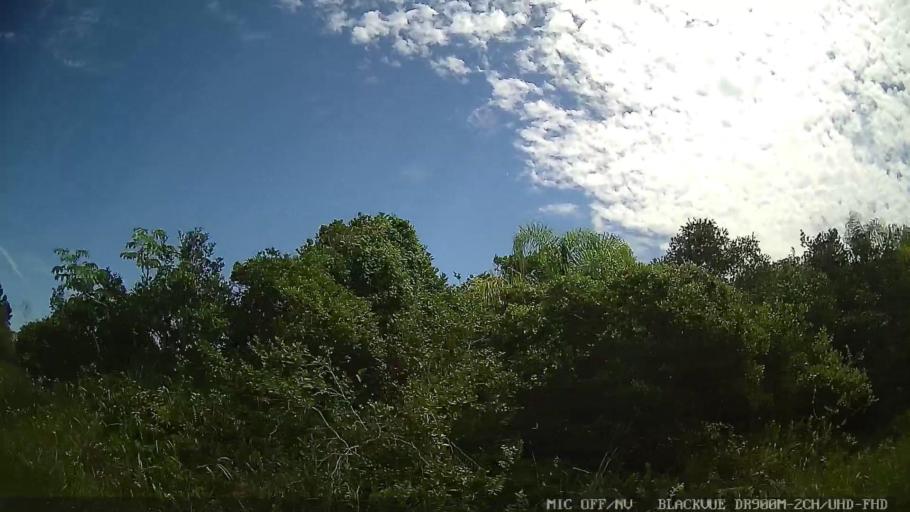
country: BR
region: Sao Paulo
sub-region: Iguape
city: Iguape
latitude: -24.7176
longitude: -47.5082
